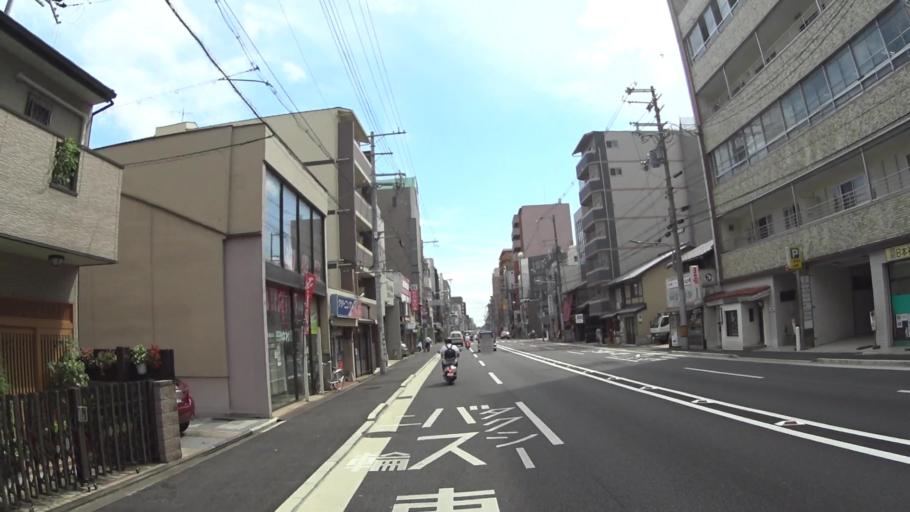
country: JP
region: Kyoto
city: Kyoto
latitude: 35.0009
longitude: 135.7491
